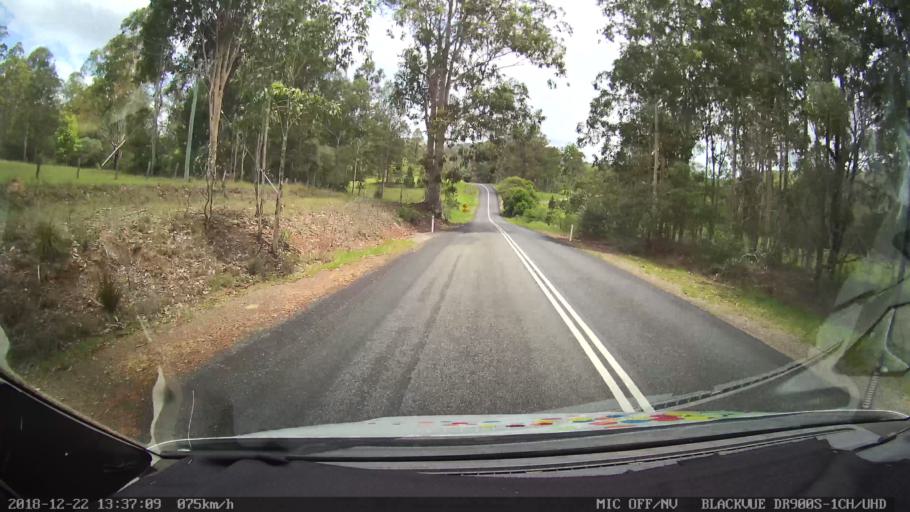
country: AU
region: New South Wales
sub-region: Clarence Valley
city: Coutts Crossing
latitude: -29.8870
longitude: 152.7893
